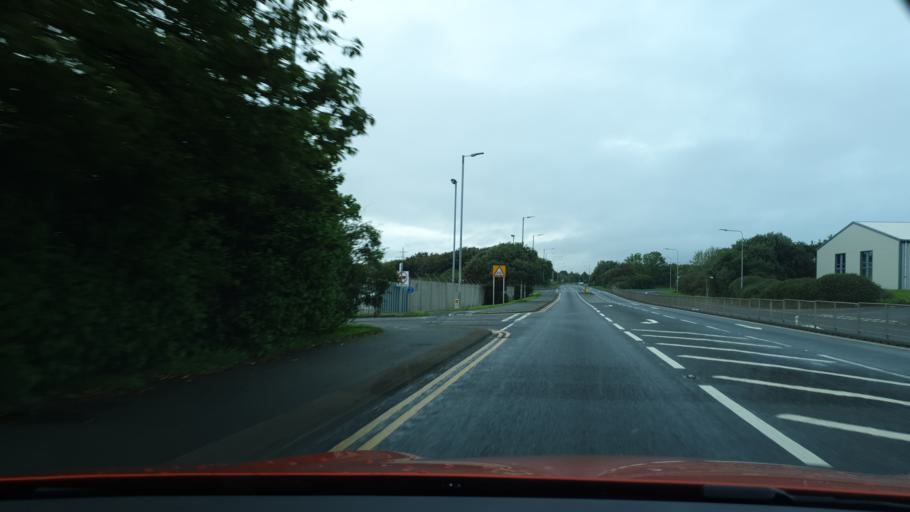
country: GB
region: England
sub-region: Cumbria
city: Barrow in Furness
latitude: 54.1452
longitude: -3.2305
